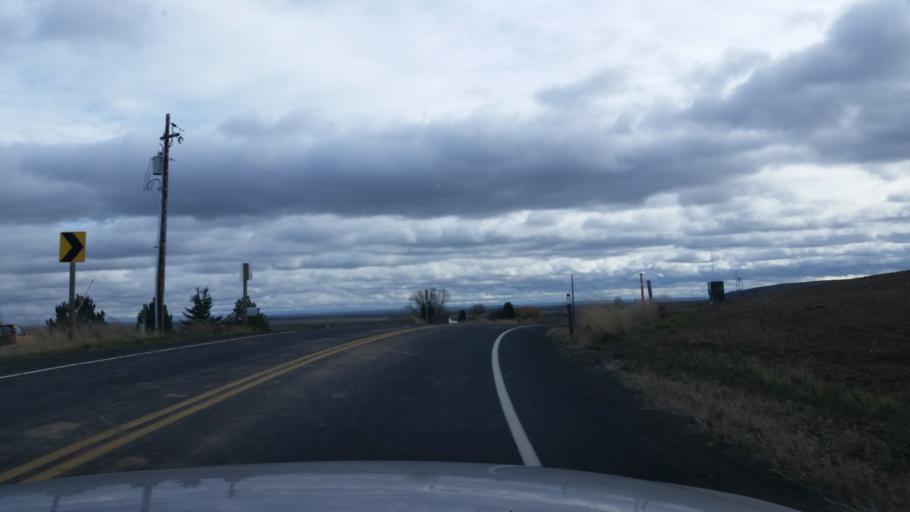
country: US
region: Washington
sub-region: Lincoln County
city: Davenport
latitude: 47.3422
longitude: -118.0052
